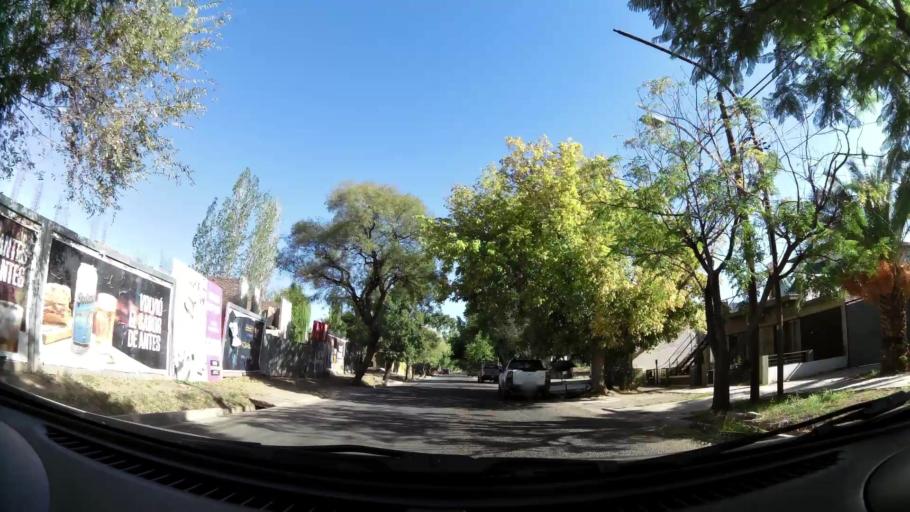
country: AR
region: Mendoza
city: Mendoza
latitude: -32.9010
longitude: -68.8172
